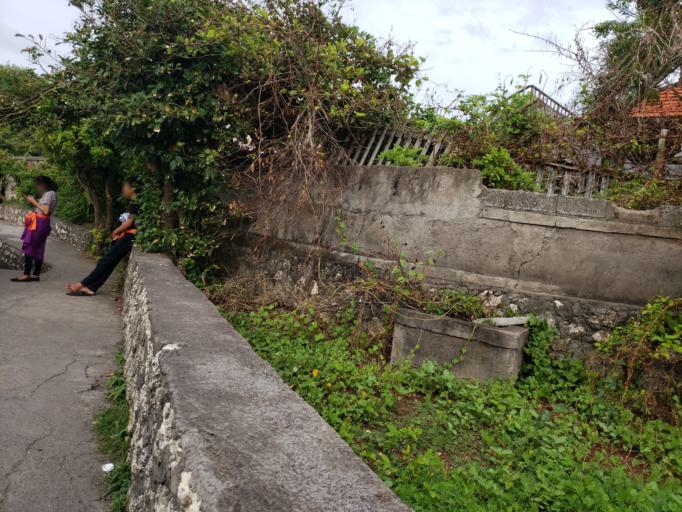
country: ID
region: Bali
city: Pecatu
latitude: -8.8308
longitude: 115.0853
